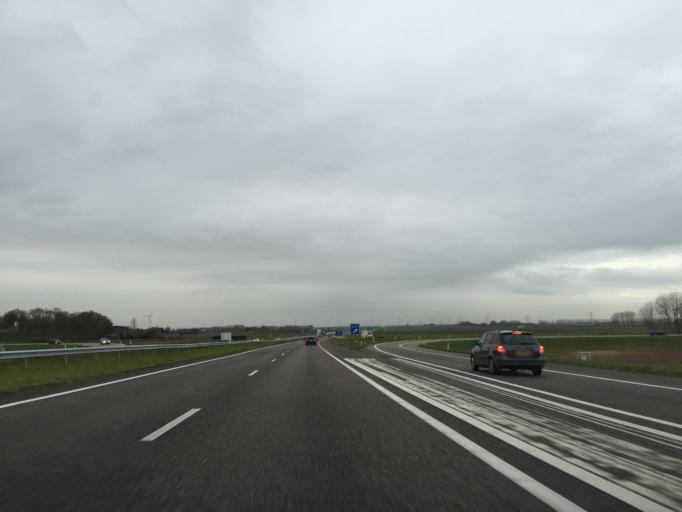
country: NL
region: North Brabant
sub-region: Gemeente Woensdrecht
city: Woensdrecht
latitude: 51.4412
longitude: 4.3107
